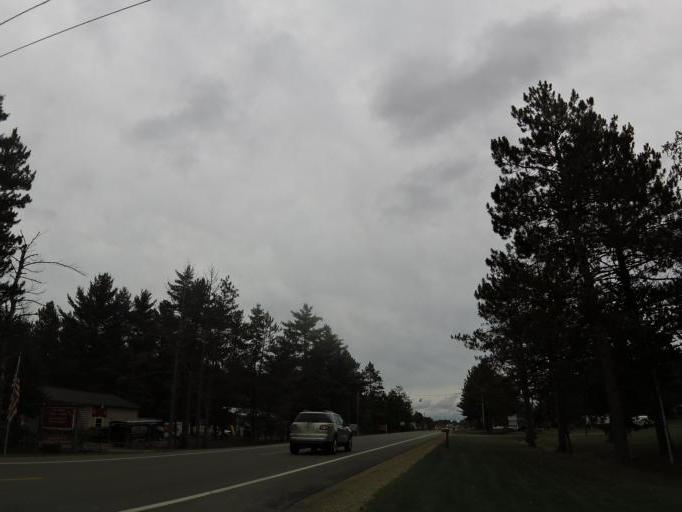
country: US
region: Michigan
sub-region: Roscommon County
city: Roscommon
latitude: 44.5059
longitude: -84.6052
